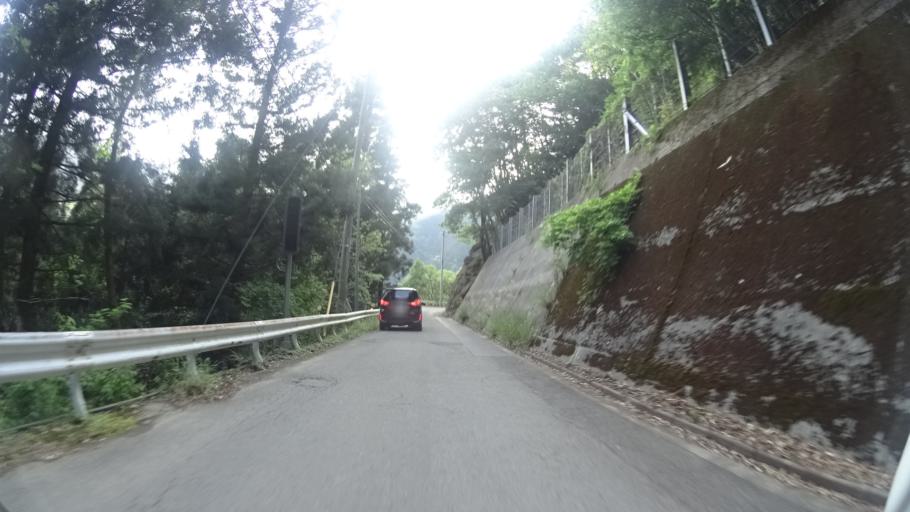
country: JP
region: Tokushima
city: Ikedacho
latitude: 33.9451
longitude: 133.8200
